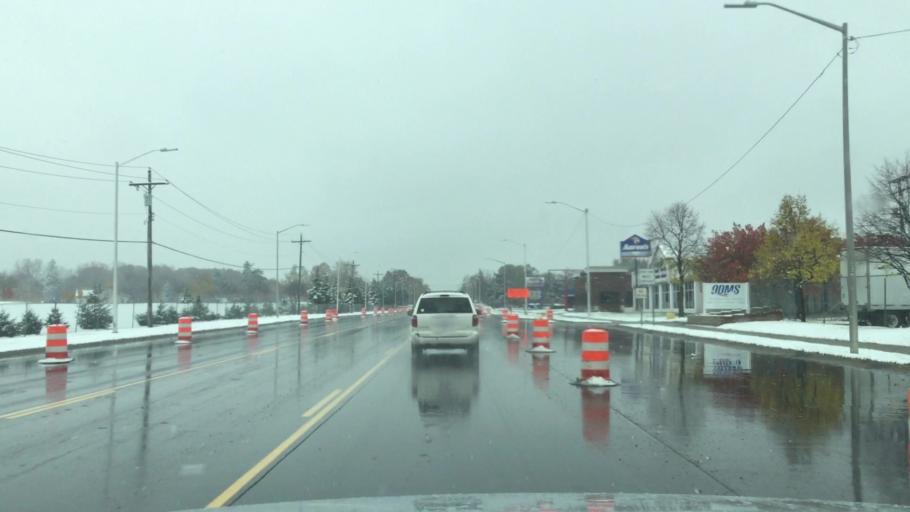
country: US
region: Michigan
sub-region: Oakland County
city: Pontiac
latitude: 42.6609
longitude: -83.2711
